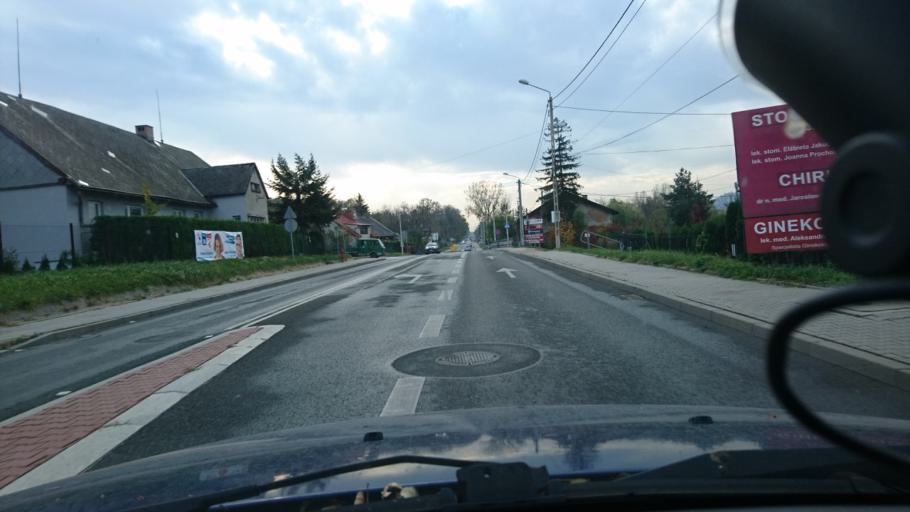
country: PL
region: Silesian Voivodeship
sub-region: Bielsko-Biala
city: Bielsko-Biala
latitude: 49.7969
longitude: 19.0636
